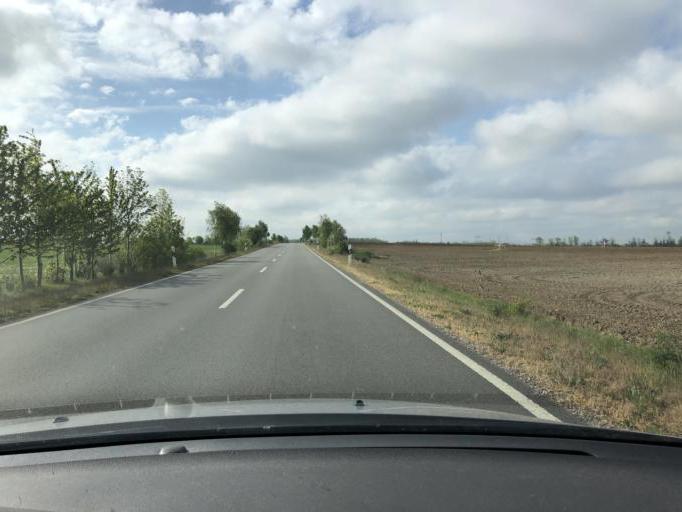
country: DE
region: Saxony
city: Neukieritzsch
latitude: 51.1636
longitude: 12.4185
